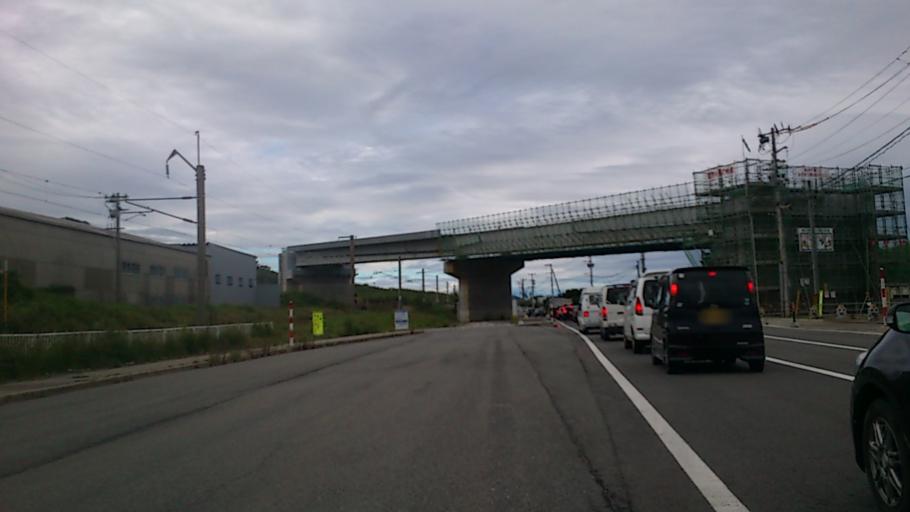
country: JP
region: Akita
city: Akita Shi
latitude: 39.6410
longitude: 140.0656
